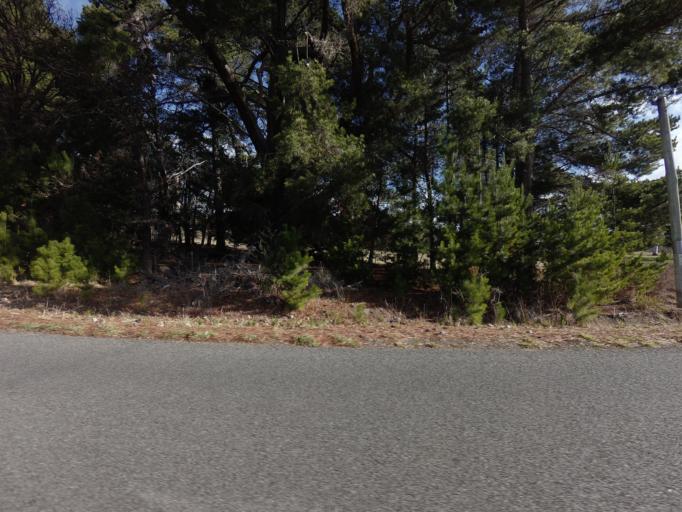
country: AU
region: Tasmania
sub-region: Derwent Valley
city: New Norfolk
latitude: -42.6520
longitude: 146.7683
